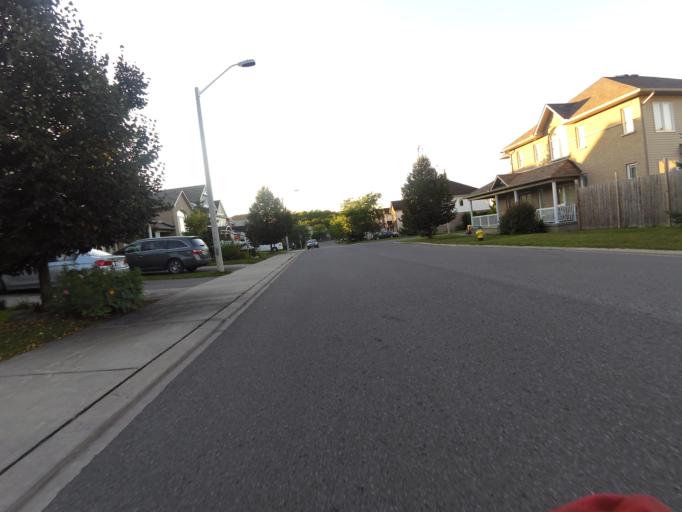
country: CA
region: Ontario
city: Bells Corners
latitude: 45.3473
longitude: -75.9468
